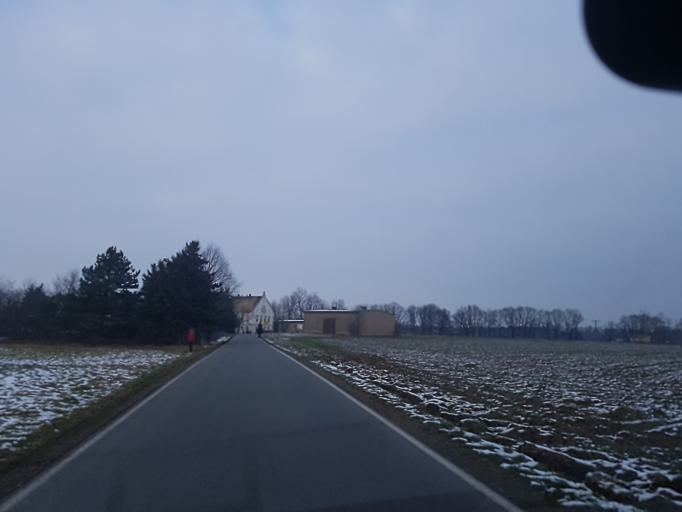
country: DE
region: Saxony
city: Cavertitz
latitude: 51.3841
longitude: 13.1567
